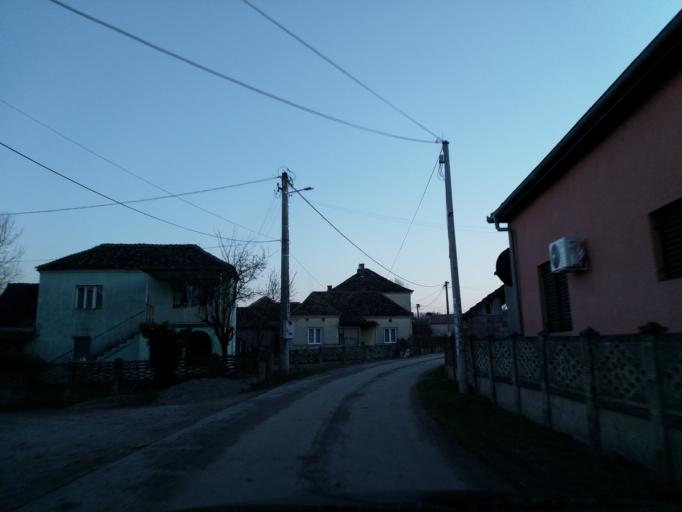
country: RS
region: Central Serbia
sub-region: Pomoravski Okrug
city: Paracin
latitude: 43.8635
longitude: 21.4743
